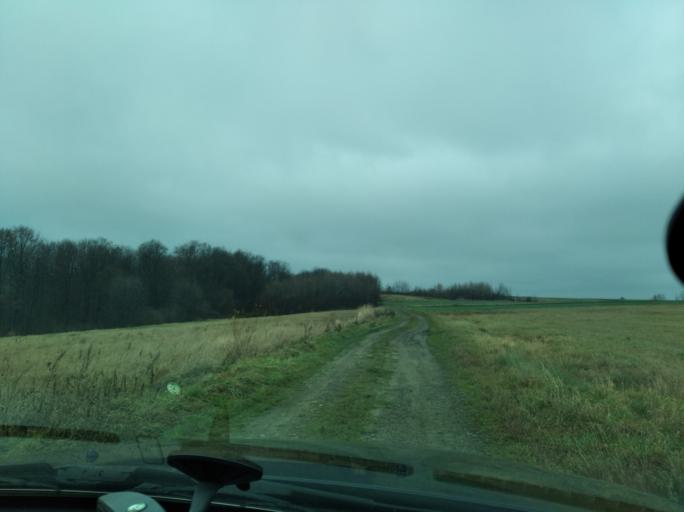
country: PL
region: Subcarpathian Voivodeship
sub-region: Powiat przeworski
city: Jawornik Polski
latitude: 49.8930
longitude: 22.2761
